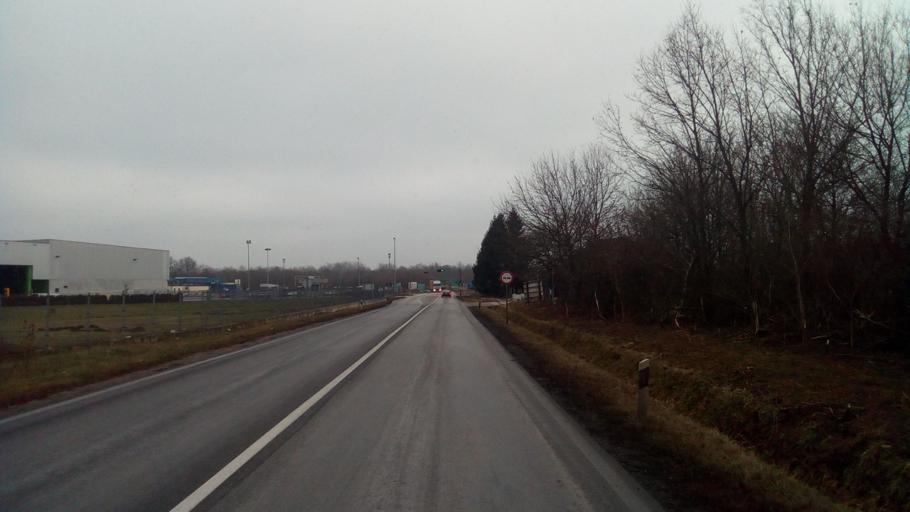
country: HR
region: Zagrebacka
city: Jastrebarsko
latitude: 45.6468
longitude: 15.6717
